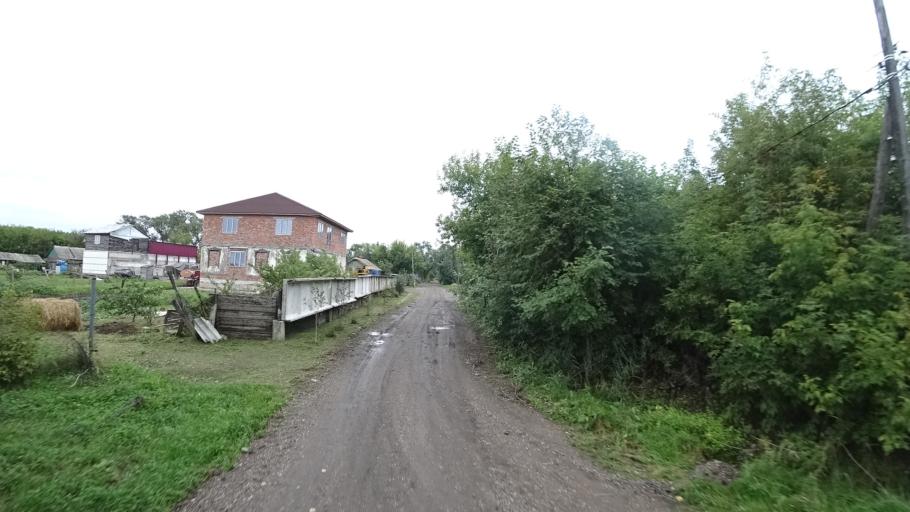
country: RU
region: Primorskiy
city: Chernigovka
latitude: 44.3385
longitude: 132.5411
